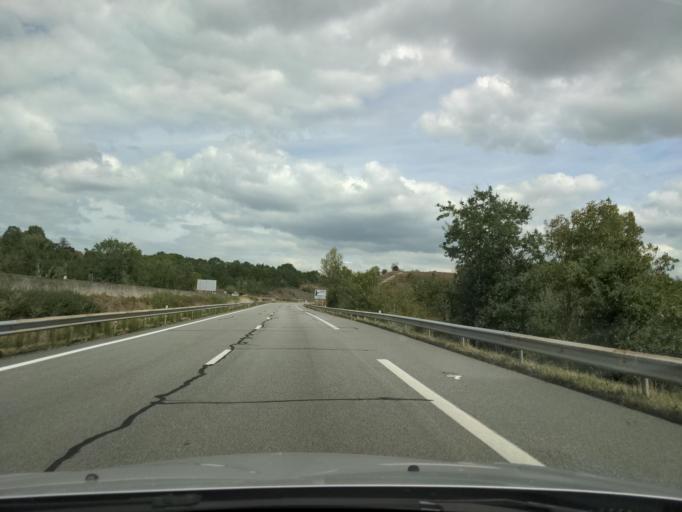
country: FR
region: Limousin
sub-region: Departement de la Creuse
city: Ajain
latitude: 46.1917
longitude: 1.9534
